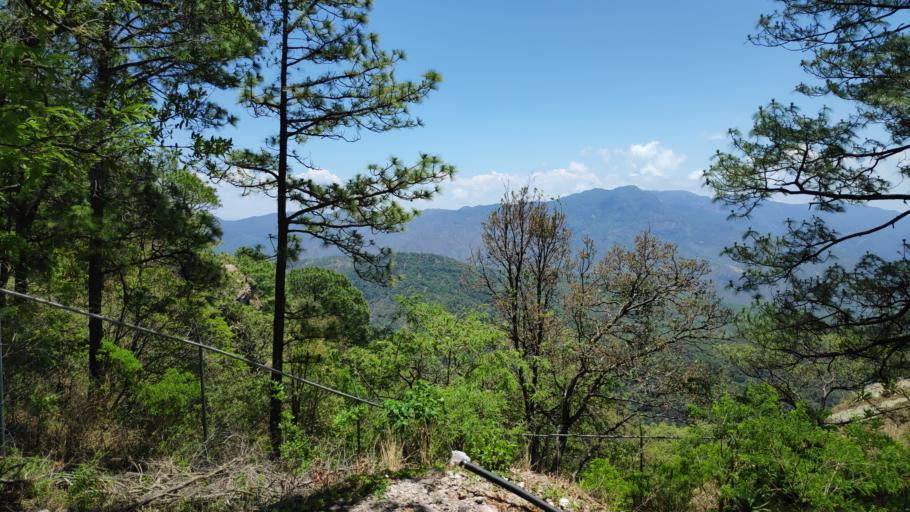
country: MX
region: Sinaloa
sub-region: Sinaloa
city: Bacubirito
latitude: 25.7458
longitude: -107.5507
